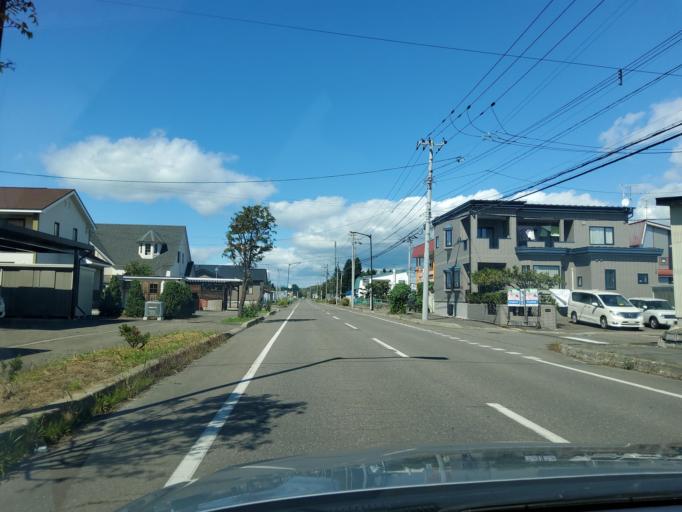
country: JP
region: Hokkaido
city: Obihiro
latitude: 42.9490
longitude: 143.2154
